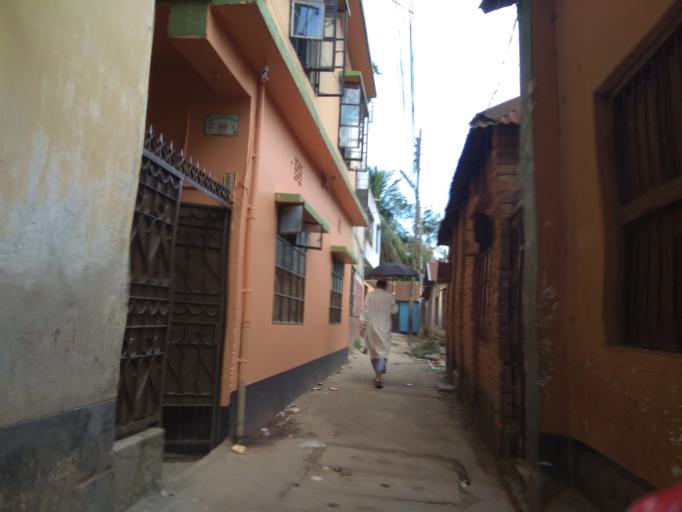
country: BD
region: Dhaka
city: Tungi
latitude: 23.8261
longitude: 90.3907
